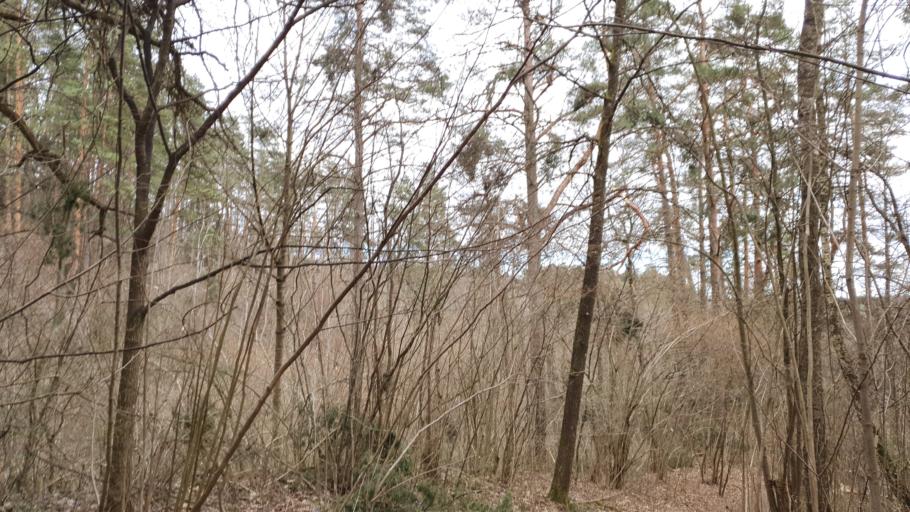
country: LT
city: Grigiskes
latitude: 54.7370
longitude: 25.0257
